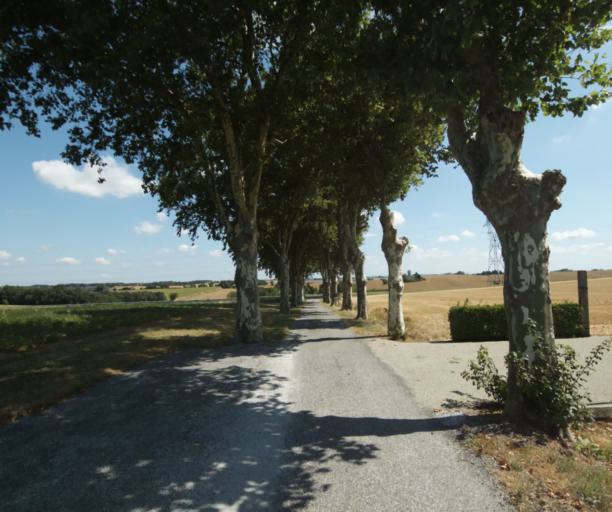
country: FR
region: Midi-Pyrenees
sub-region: Departement de la Haute-Garonne
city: Auriac-sur-Vendinelle
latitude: 43.4623
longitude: 1.8139
